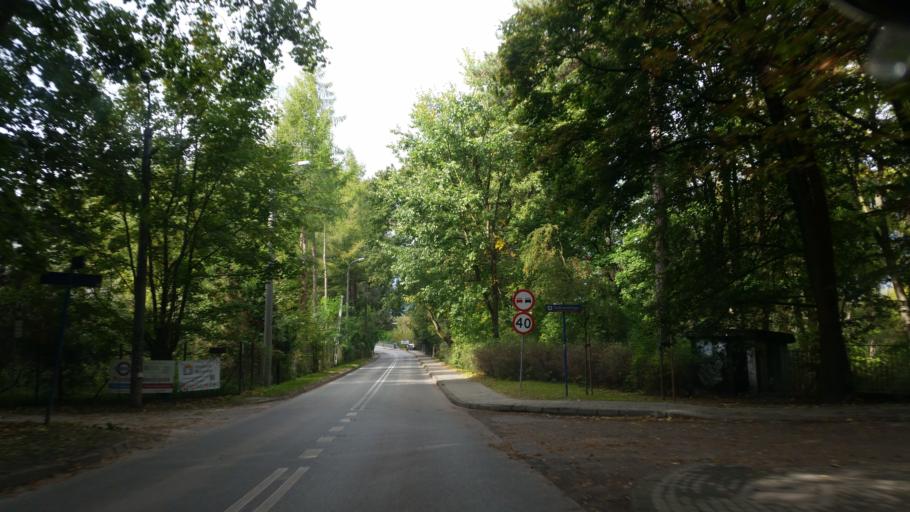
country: PL
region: Masovian Voivodeship
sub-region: Powiat piaseczynski
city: Konstancin-Jeziorna
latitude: 52.0812
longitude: 21.0966
